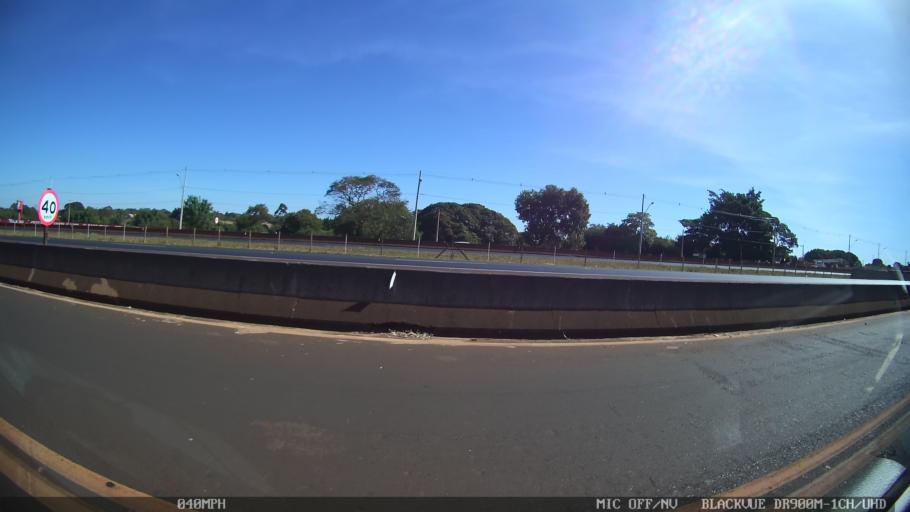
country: BR
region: Sao Paulo
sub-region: Barretos
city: Barretos
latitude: -20.5535
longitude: -48.5907
